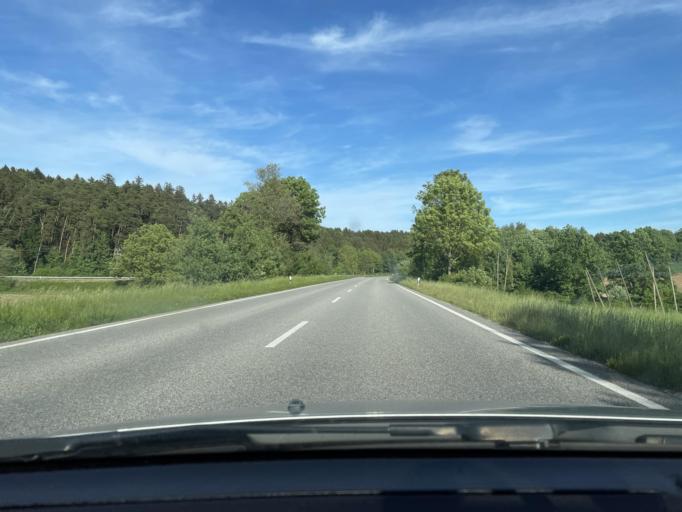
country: DE
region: Bavaria
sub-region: Lower Bavaria
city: Pfeffenhausen
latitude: 48.6530
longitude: 11.9653
